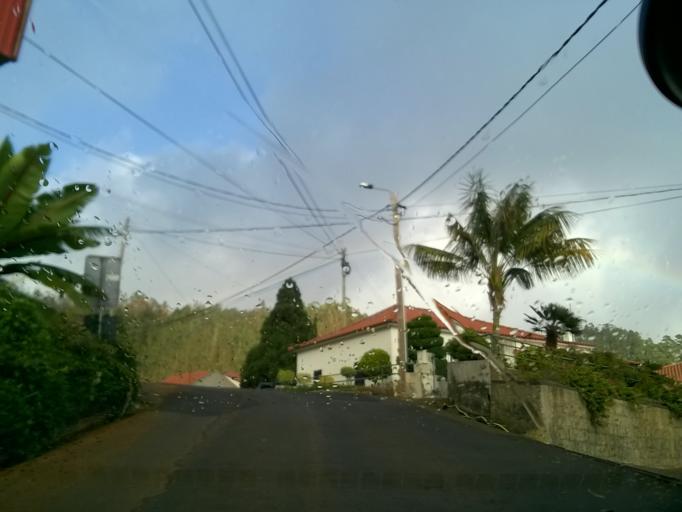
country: PT
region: Madeira
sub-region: Santa Cruz
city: Camacha
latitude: 32.6649
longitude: -16.8648
